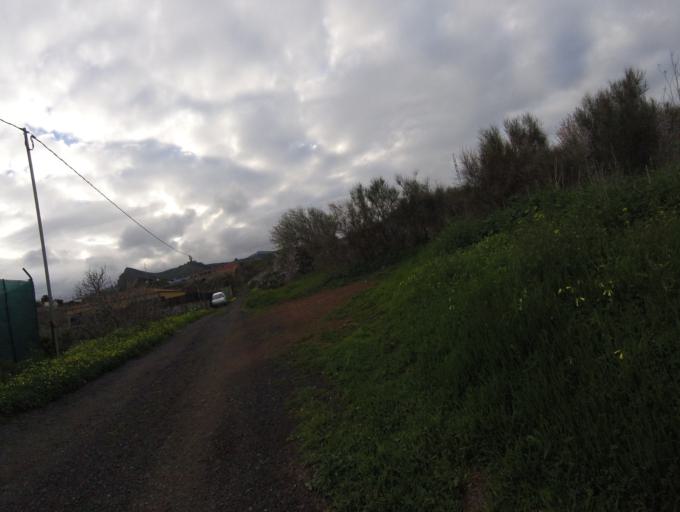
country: ES
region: Canary Islands
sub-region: Provincia de Santa Cruz de Tenerife
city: La Laguna
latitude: 28.4481
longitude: -16.3375
